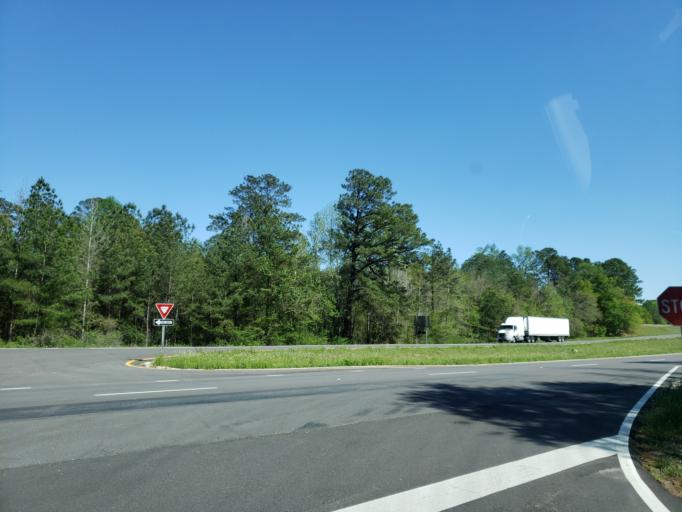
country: US
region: Mississippi
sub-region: Stone County
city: Wiggins
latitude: 30.8649
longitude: -89.1648
